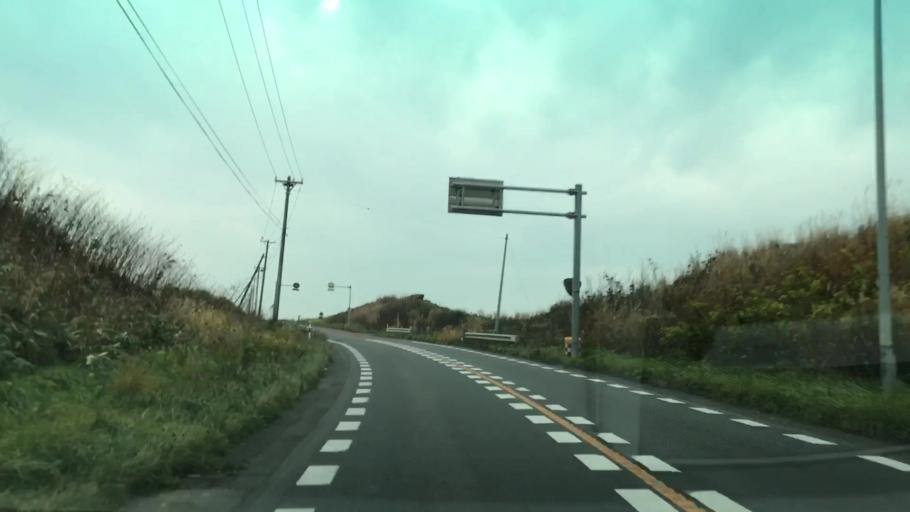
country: JP
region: Hokkaido
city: Ishikari
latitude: 43.3537
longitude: 141.4281
